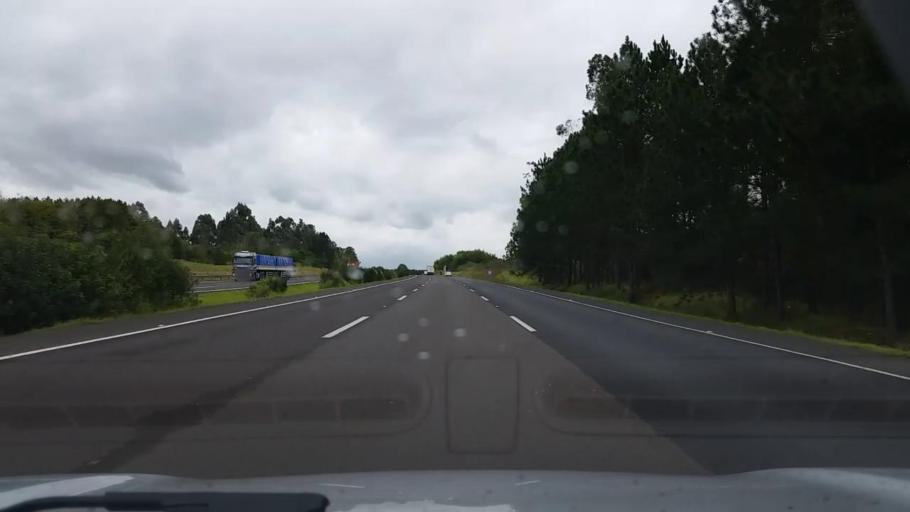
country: BR
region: Rio Grande do Sul
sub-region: Gravatai
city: Gravatai
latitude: -29.9232
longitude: -50.8528
